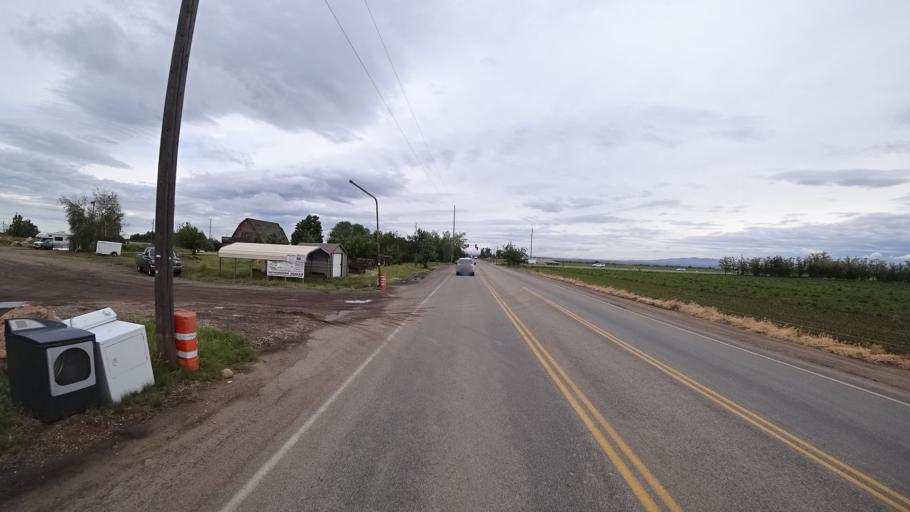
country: US
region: Idaho
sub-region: Ada County
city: Star
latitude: 43.6618
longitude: -116.4935
